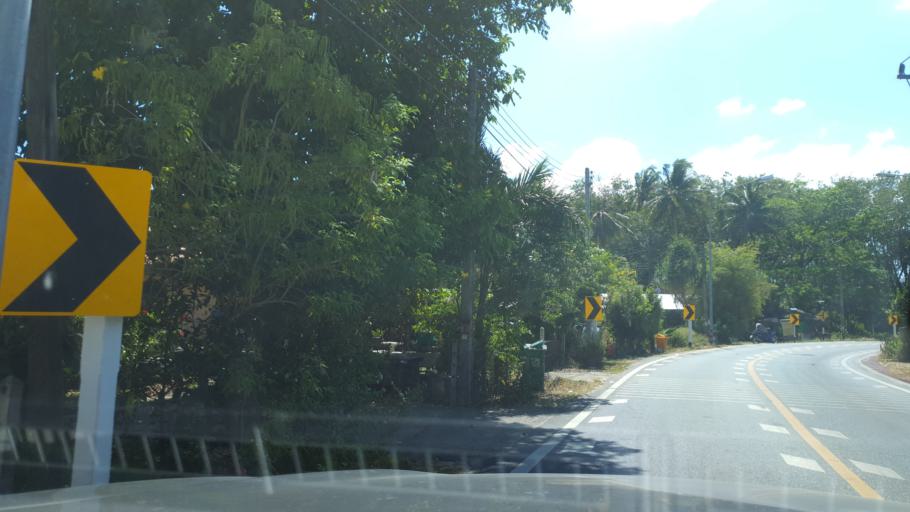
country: TH
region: Phuket
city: Thalang
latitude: 8.1232
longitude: 98.3112
